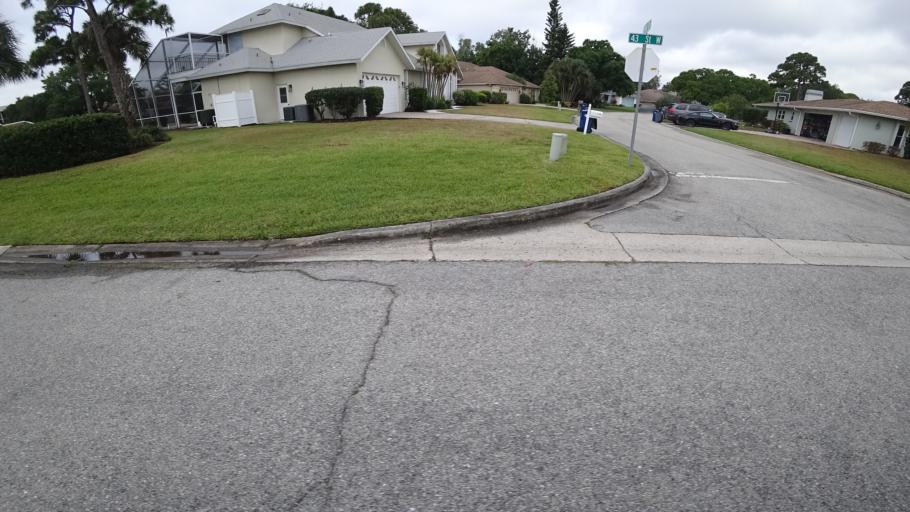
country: US
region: Florida
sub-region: Manatee County
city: Bayshore Gardens
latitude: 27.4336
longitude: -82.6020
